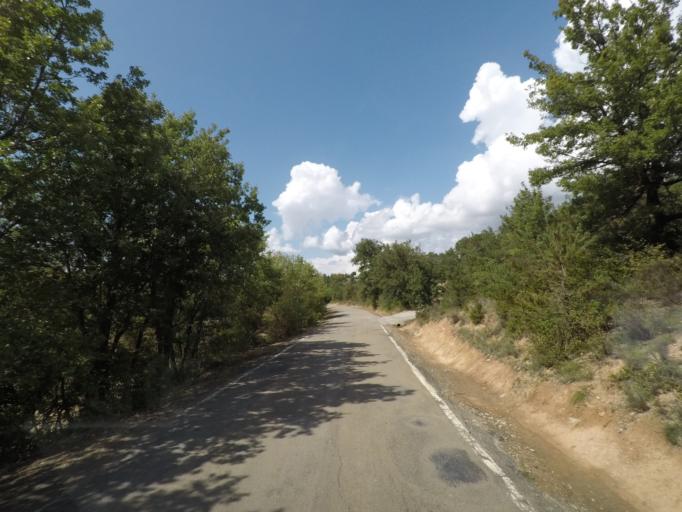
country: ES
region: Aragon
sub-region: Provincia de Huesca
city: Arguis
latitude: 42.4037
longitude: -0.3809
